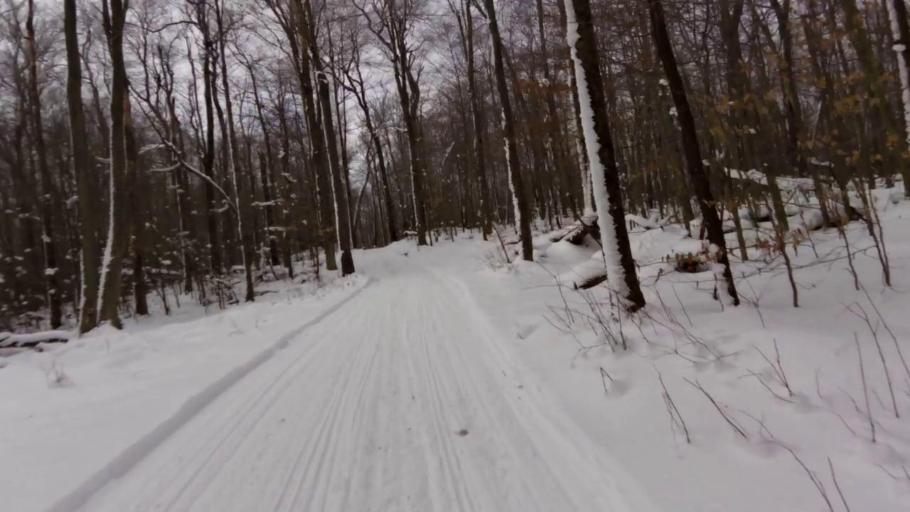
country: US
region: New York
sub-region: Cattaraugus County
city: Salamanca
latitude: 42.0330
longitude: -78.7490
